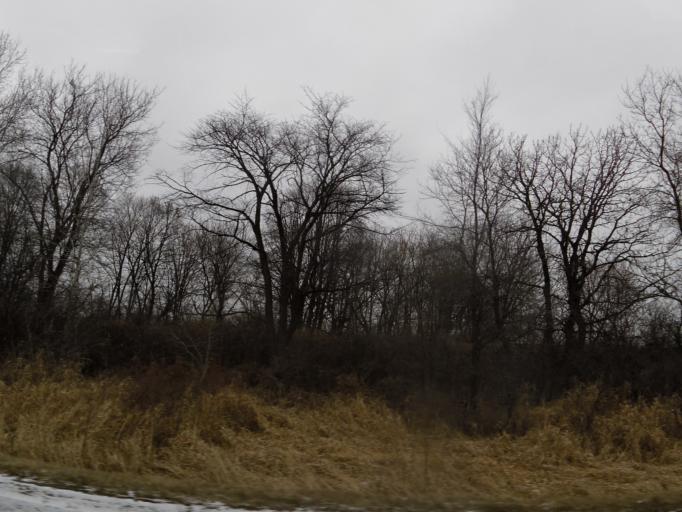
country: US
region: Minnesota
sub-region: Hennepin County
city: Independence
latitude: 45.0142
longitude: -93.6931
